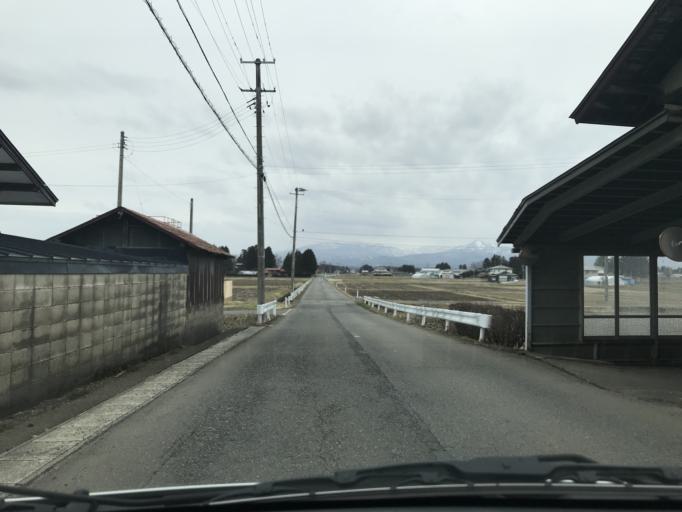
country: JP
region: Iwate
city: Kitakami
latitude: 39.3169
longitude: 141.0645
